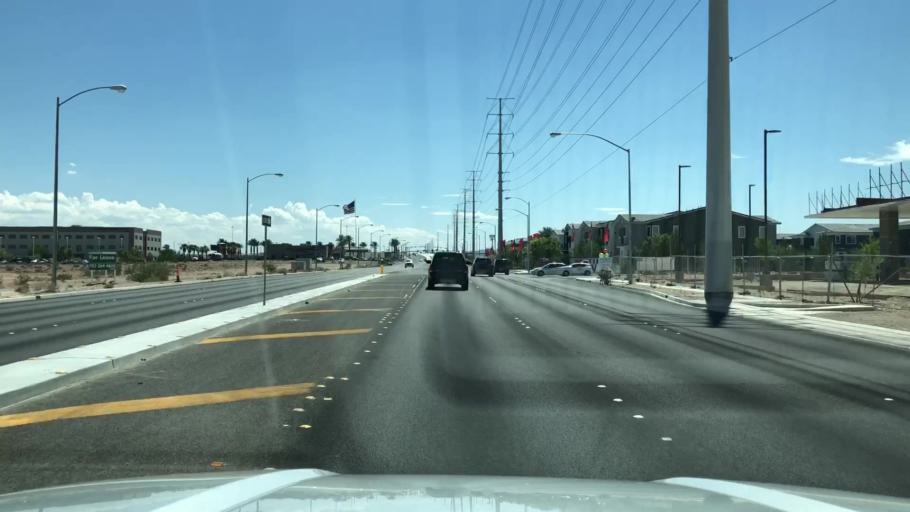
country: US
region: Nevada
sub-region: Clark County
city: Spring Valley
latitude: 36.0748
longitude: -115.2795
